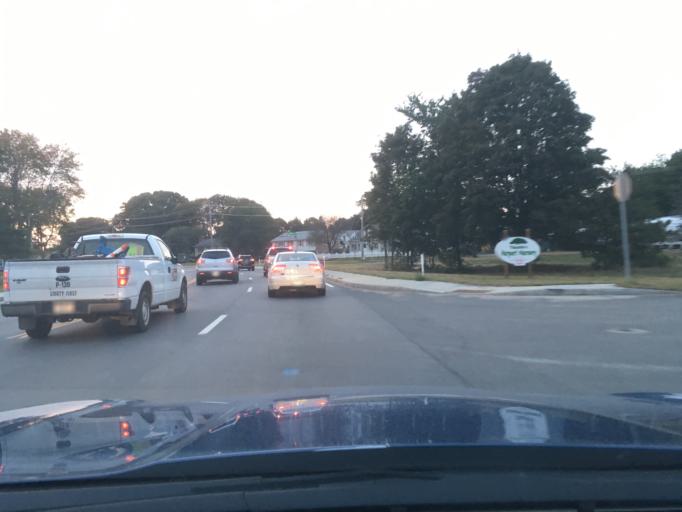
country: US
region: Rhode Island
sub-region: Kent County
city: Warwick
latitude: 41.7098
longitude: -71.4417
